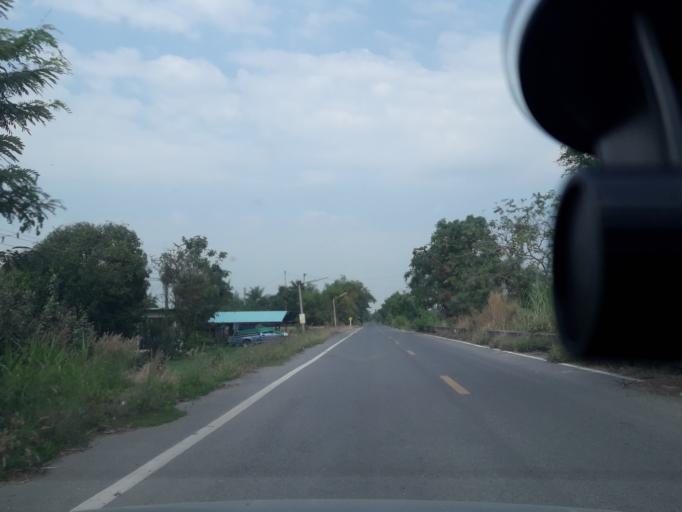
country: TH
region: Sara Buri
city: Nong Khae
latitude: 14.2290
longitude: 100.8914
